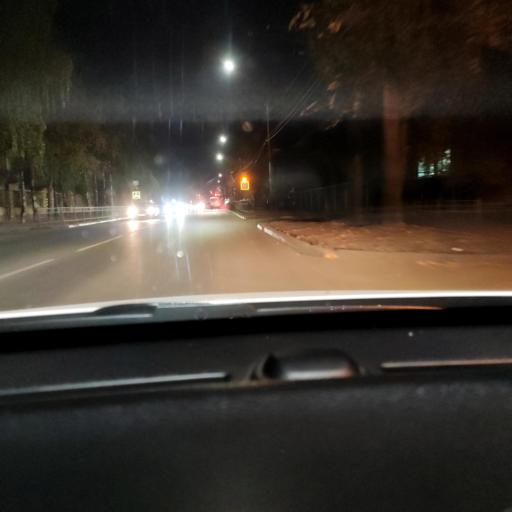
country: RU
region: Voronezj
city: Voronezh
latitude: 51.7216
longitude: 39.2685
